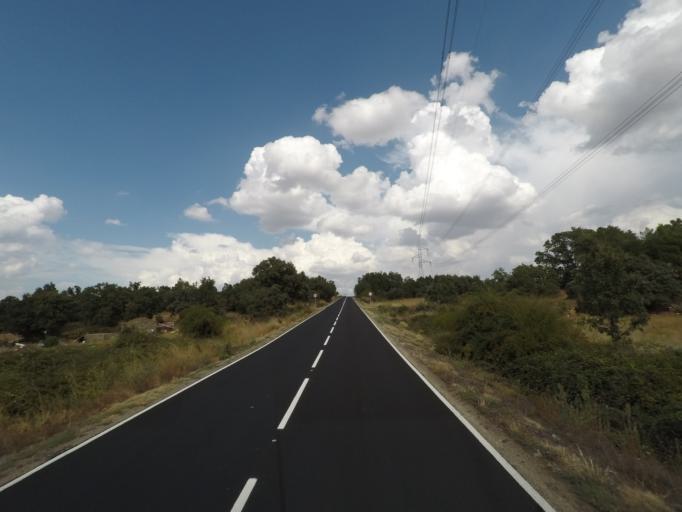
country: ES
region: Castille and Leon
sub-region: Provincia de Zamora
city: Fermoselle
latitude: 41.3121
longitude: -6.3100
